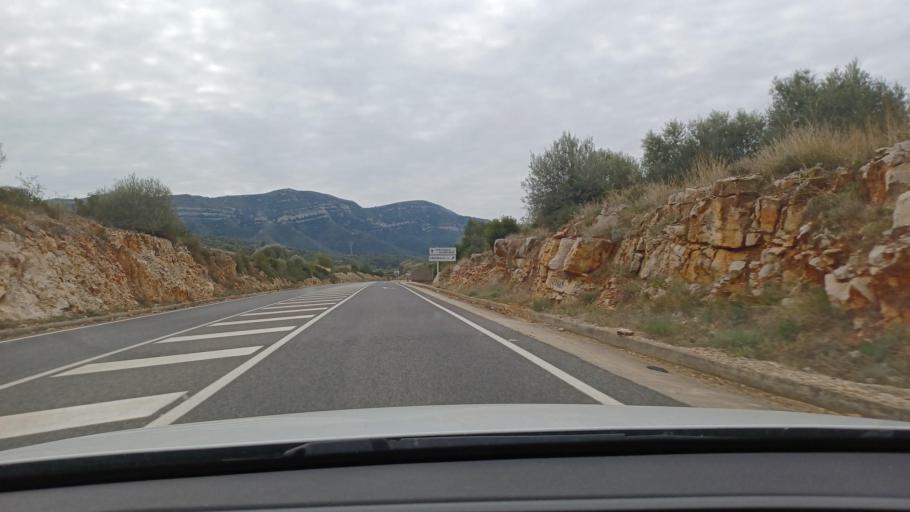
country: ES
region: Catalonia
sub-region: Provincia de Tarragona
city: Masdenverge
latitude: 40.6779
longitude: 0.5257
